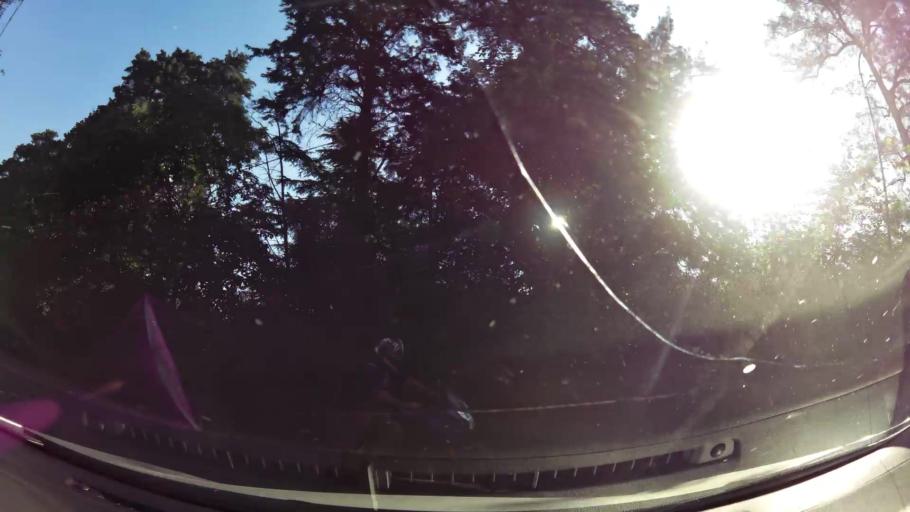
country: AR
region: Buenos Aires
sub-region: Partido de Tigre
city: Tigre
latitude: -34.4773
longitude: -58.6469
